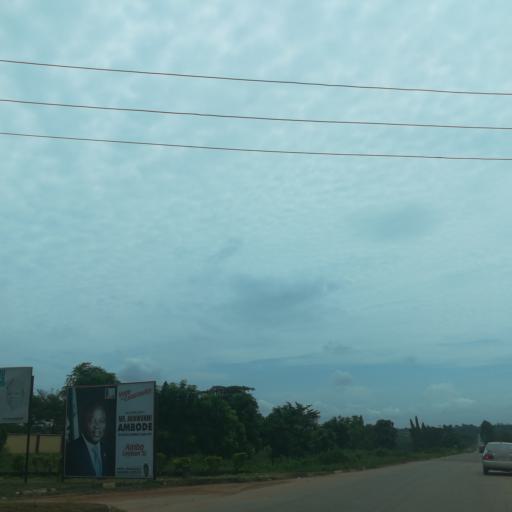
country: NG
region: Lagos
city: Ejirin
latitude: 6.6488
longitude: 3.7131
